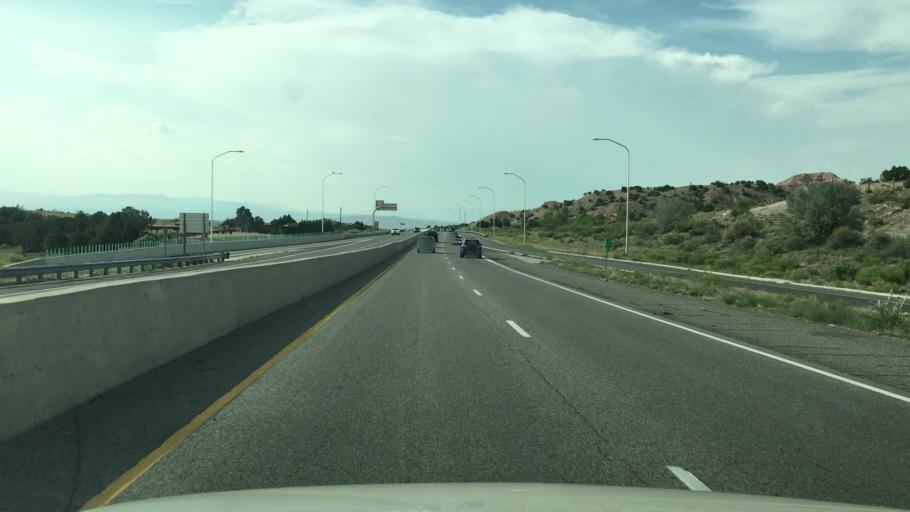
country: US
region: New Mexico
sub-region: Santa Fe County
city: Nambe
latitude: 35.8237
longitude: -105.9770
